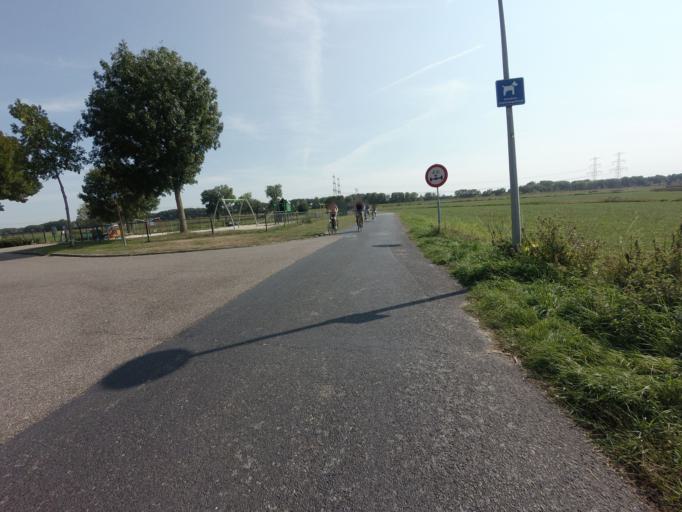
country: NL
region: Limburg
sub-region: Gemeente Maasgouw
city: Maasbracht
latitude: 51.1866
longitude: 5.9190
